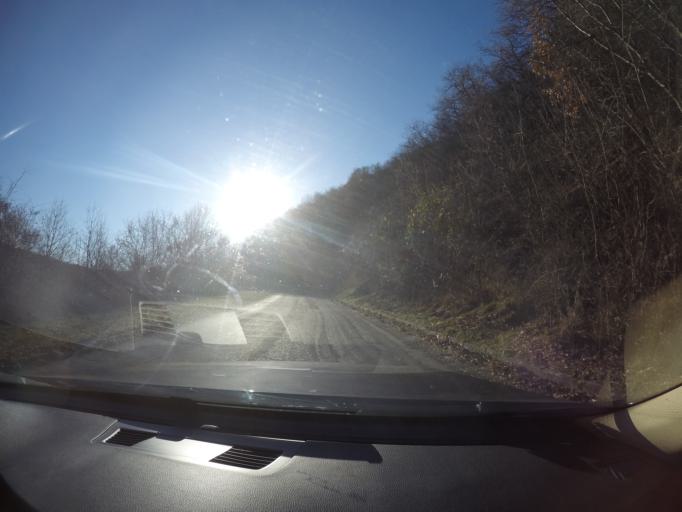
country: HU
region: Pest
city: Visegrad
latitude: 47.7960
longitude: 18.9954
